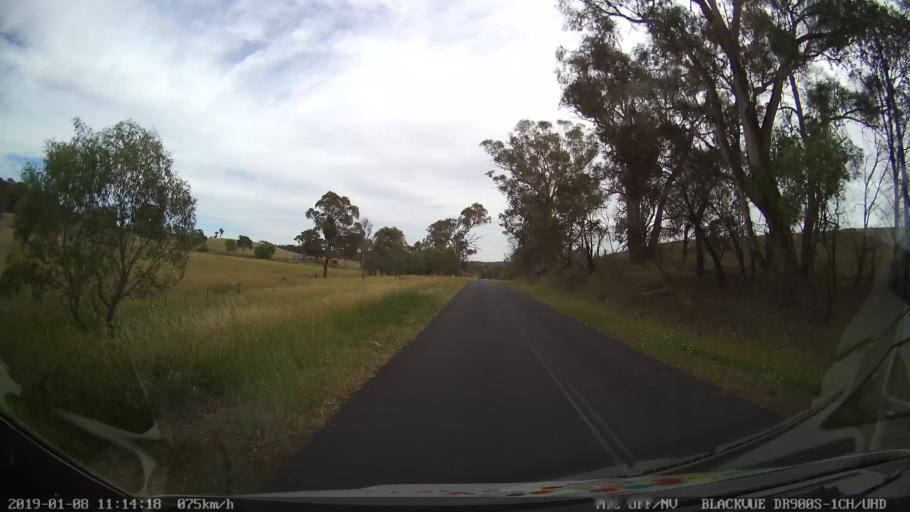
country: AU
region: New South Wales
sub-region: Guyra
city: Guyra
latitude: -30.2274
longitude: 151.5896
